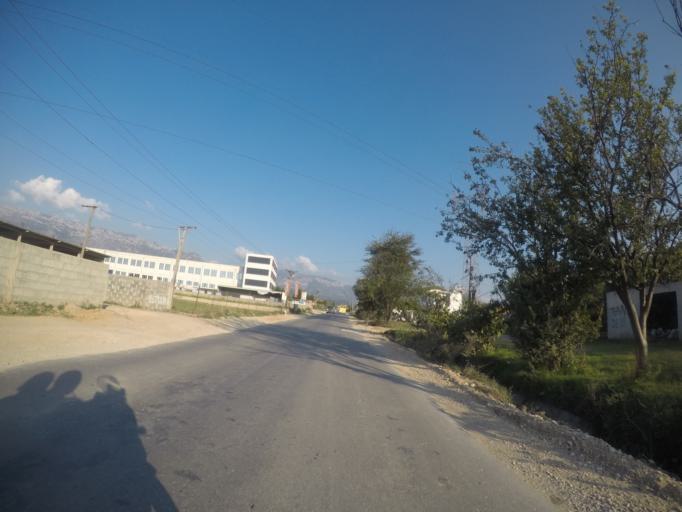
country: AL
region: Durres
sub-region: Rrethi i Krujes
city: Fushe-Kruje
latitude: 41.4773
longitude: 19.7429
